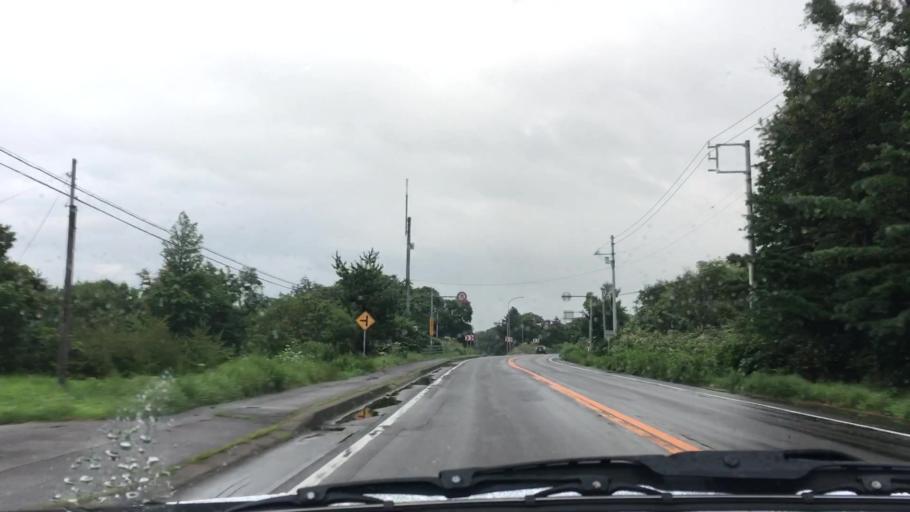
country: JP
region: Hokkaido
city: Nanae
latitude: 42.1775
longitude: 140.4492
